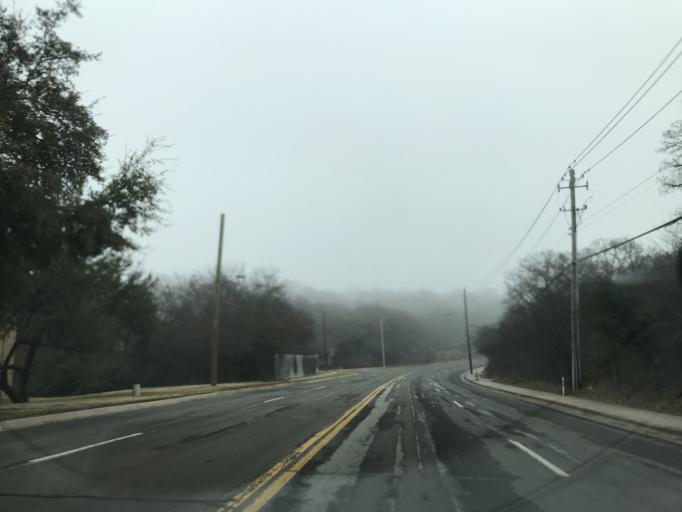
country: US
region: Texas
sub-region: Tarrant County
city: Arlington
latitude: 32.7753
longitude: -97.0926
